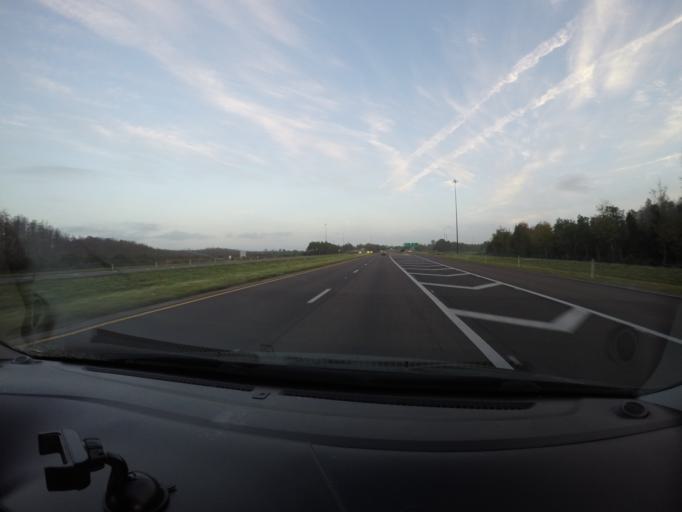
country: US
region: Florida
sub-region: Orange County
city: Conway
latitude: 28.4415
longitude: -81.2298
